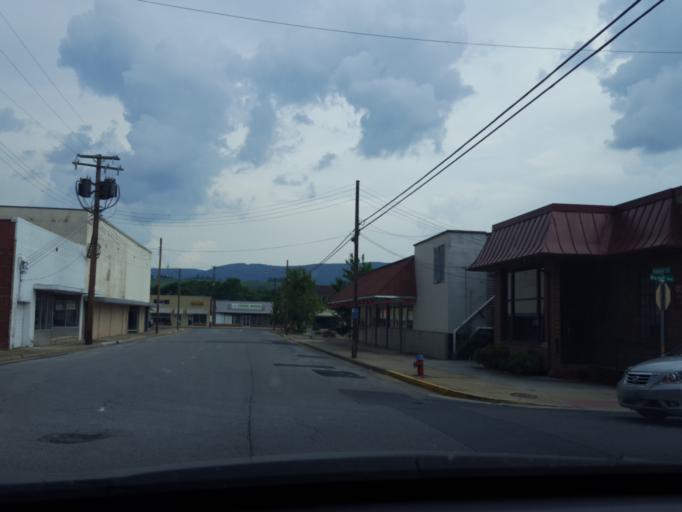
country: US
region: Virginia
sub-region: City of Waynesboro
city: Waynesboro
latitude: 38.0678
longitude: -78.8888
